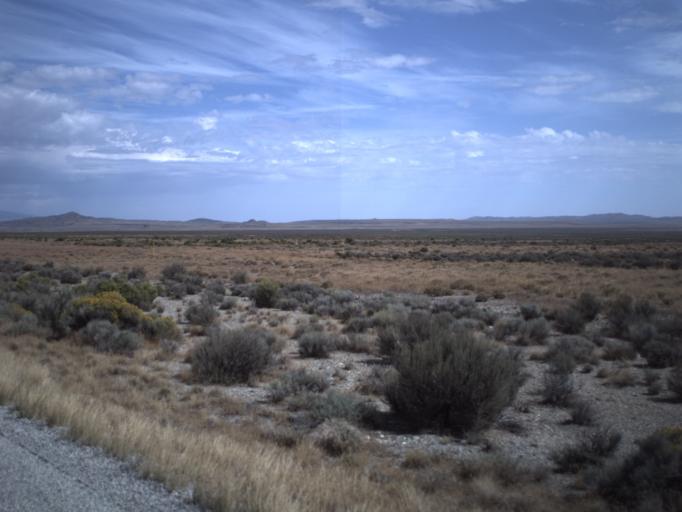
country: US
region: Utah
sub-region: Tooele County
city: Wendover
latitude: 41.5509
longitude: -113.5867
